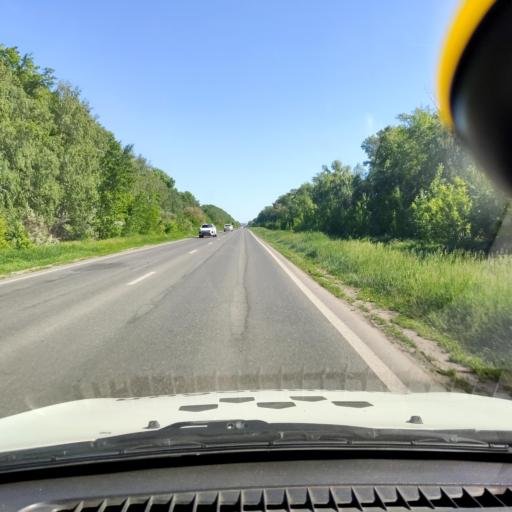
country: RU
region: Samara
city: Tol'yatti
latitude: 53.6103
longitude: 49.3163
